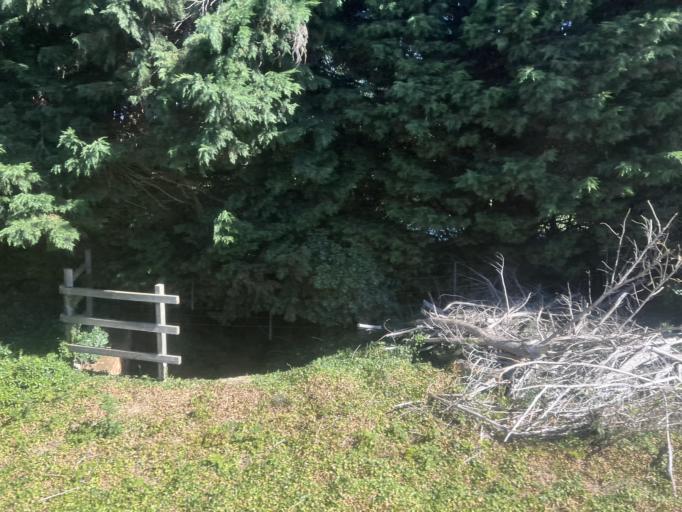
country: GB
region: England
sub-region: Lincolnshire
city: Sleaford
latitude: 52.9895
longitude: -0.3575
